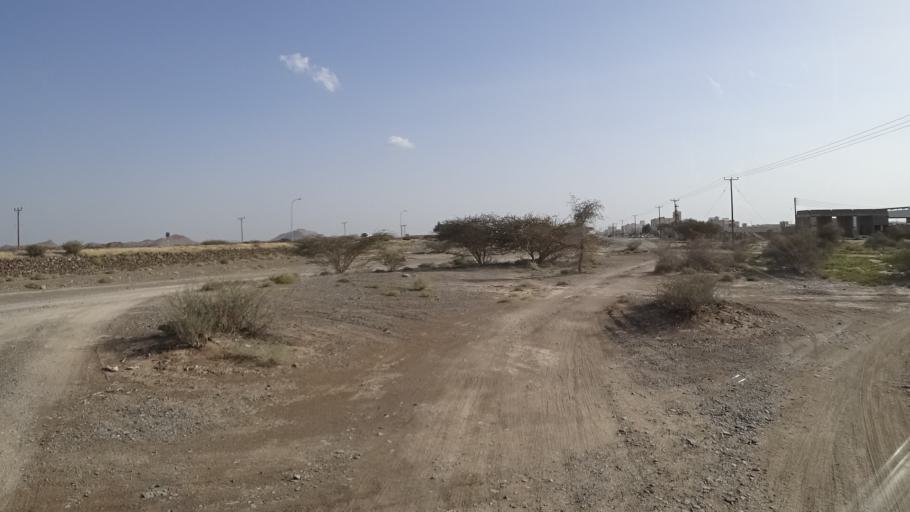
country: OM
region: Muhafazat ad Dakhiliyah
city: Izki
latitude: 22.8628
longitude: 57.7586
